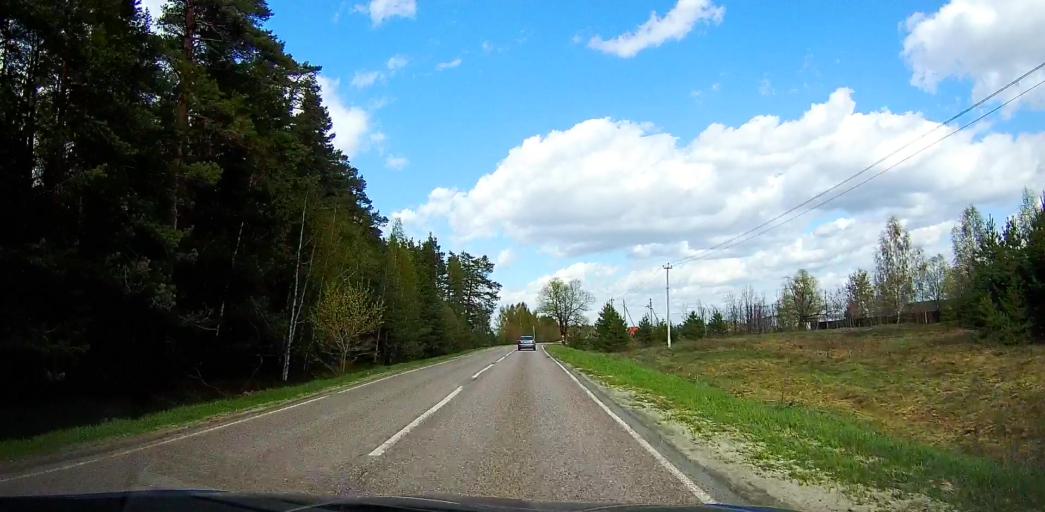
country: RU
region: Moskovskaya
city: Davydovo
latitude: 55.5974
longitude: 38.8392
